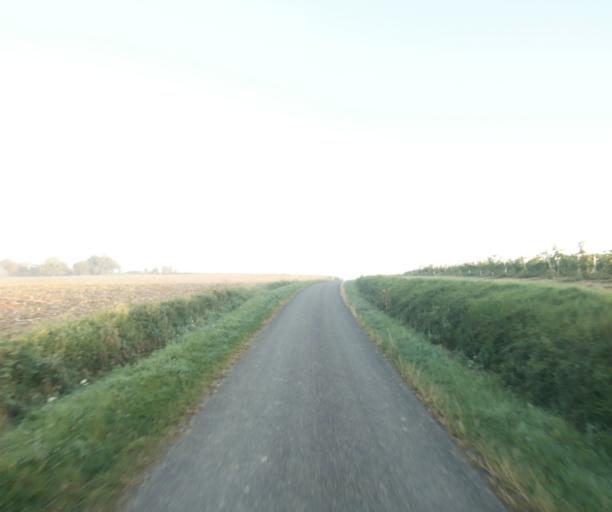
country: FR
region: Midi-Pyrenees
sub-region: Departement du Gers
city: Eauze
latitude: 43.7976
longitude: 0.1704
